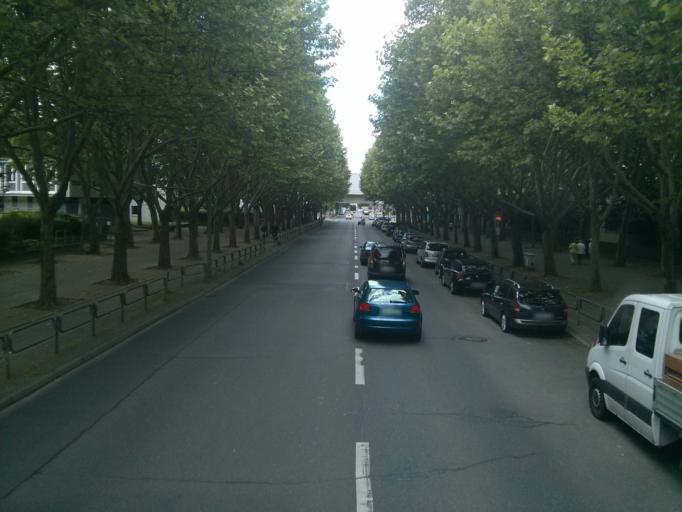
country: DE
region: Berlin
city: Markisches Viertel
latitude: 52.5967
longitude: 13.3535
